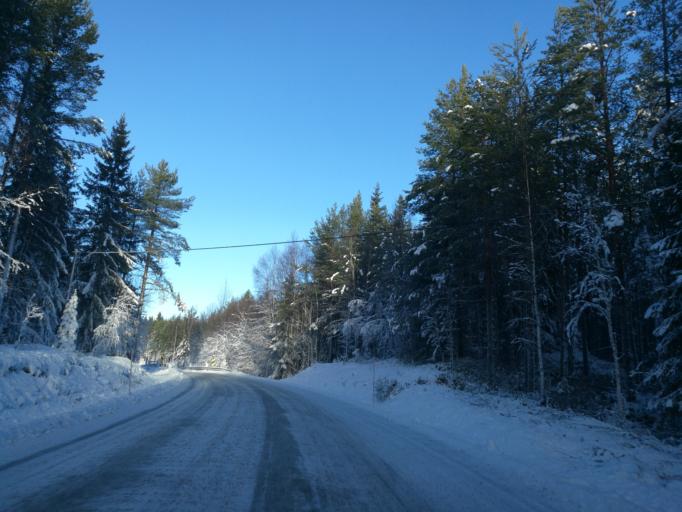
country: NO
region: Hedmark
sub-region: Grue
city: Kirkenaer
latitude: 60.4883
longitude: 12.5705
